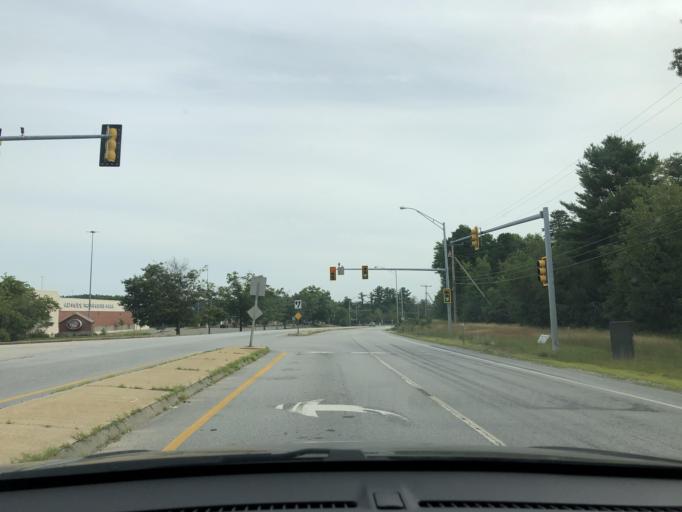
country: US
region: New Hampshire
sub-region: Merrimack County
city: Concord
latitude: 43.2201
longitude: -71.4829
